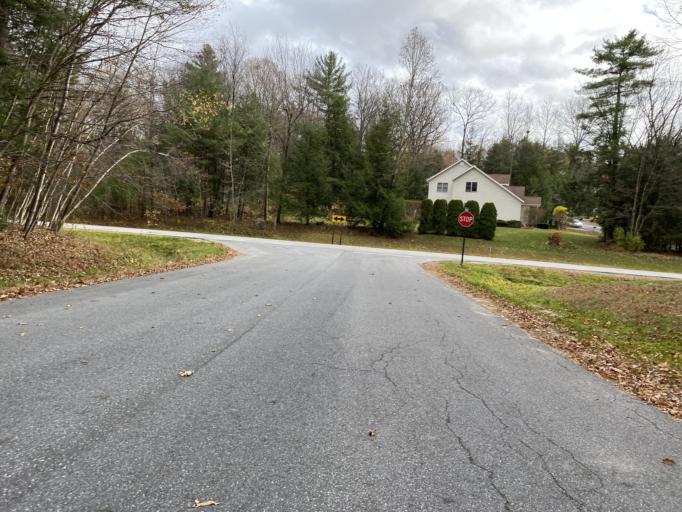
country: US
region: New York
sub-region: Saratoga County
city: Milton
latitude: 43.0959
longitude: -73.9050
